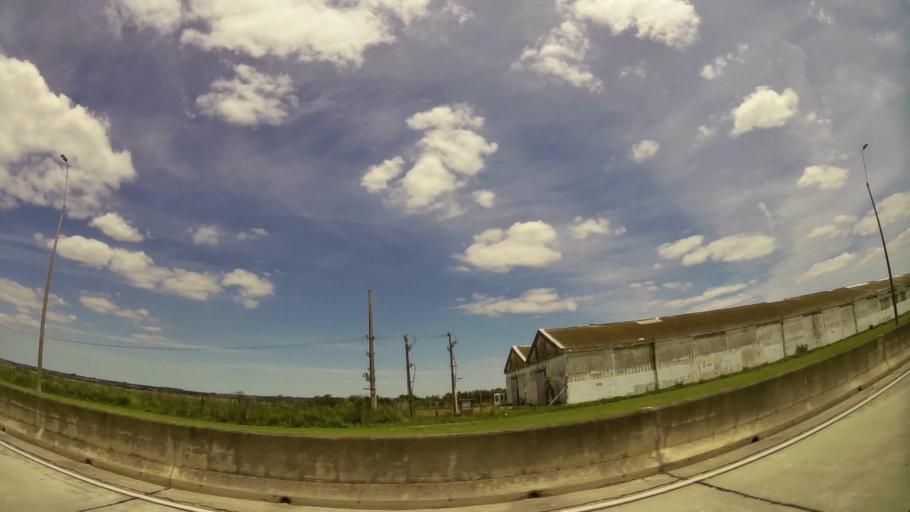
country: UY
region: San Jose
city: Delta del Tigre
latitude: -34.7715
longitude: -56.3848
